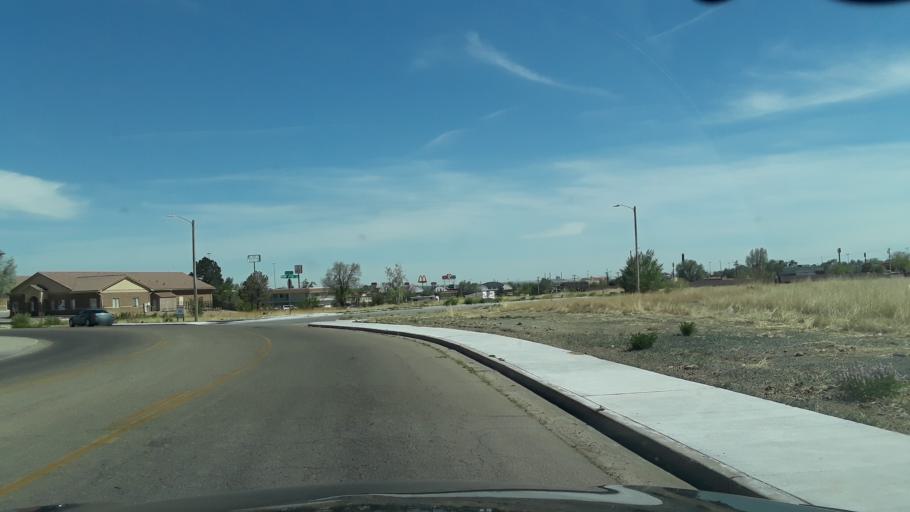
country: US
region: Colorado
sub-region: Pueblo County
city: Pueblo
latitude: 38.3122
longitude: -104.6187
